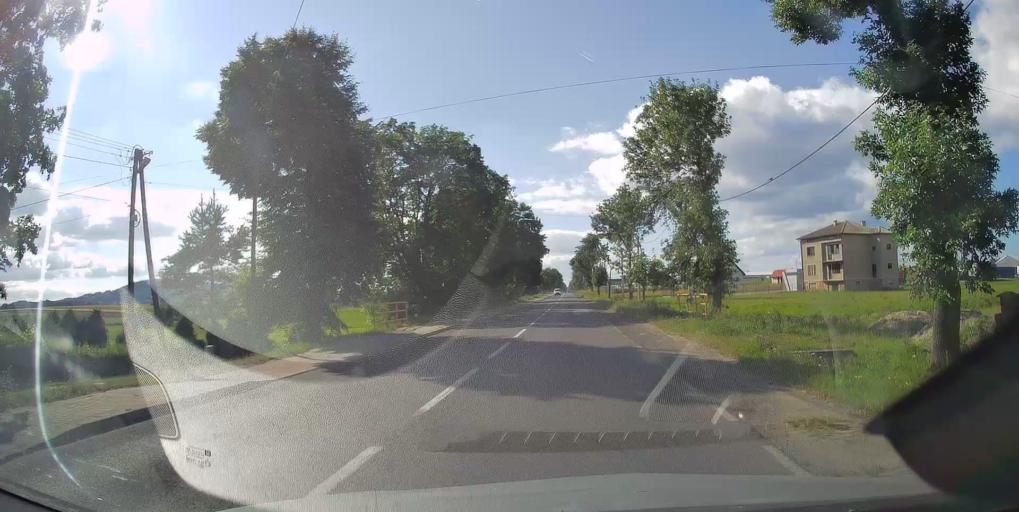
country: PL
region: Swietokrzyskie
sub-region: Powiat kielecki
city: Bodzentyn
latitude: 50.9477
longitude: 20.9341
